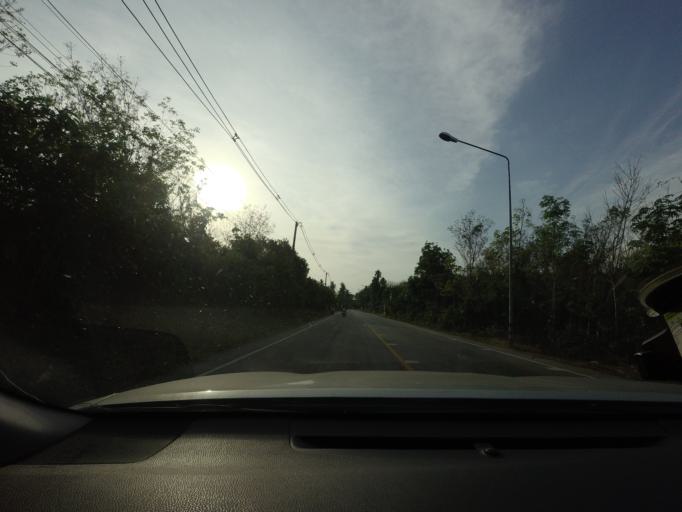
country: TH
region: Narathiwat
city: Ra-ngae
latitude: 6.3390
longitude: 101.7094
